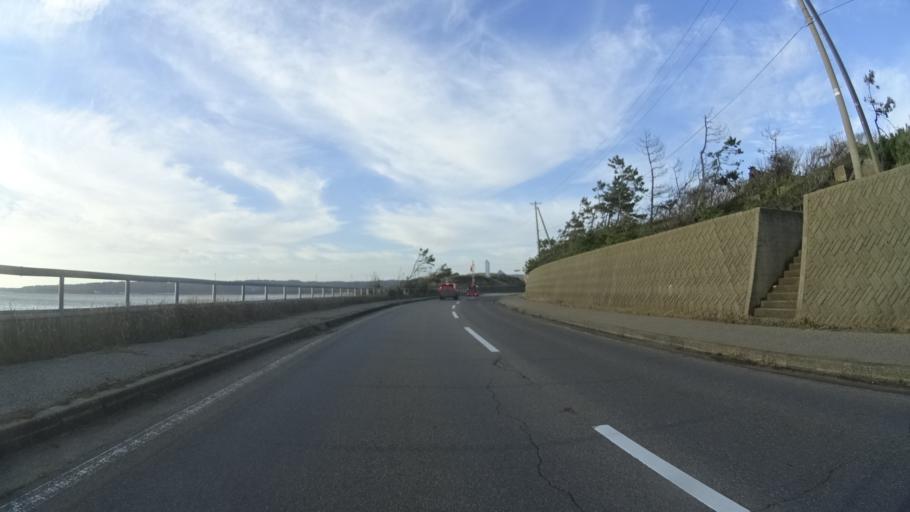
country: JP
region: Ishikawa
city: Nanao
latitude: 37.1373
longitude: 136.7262
